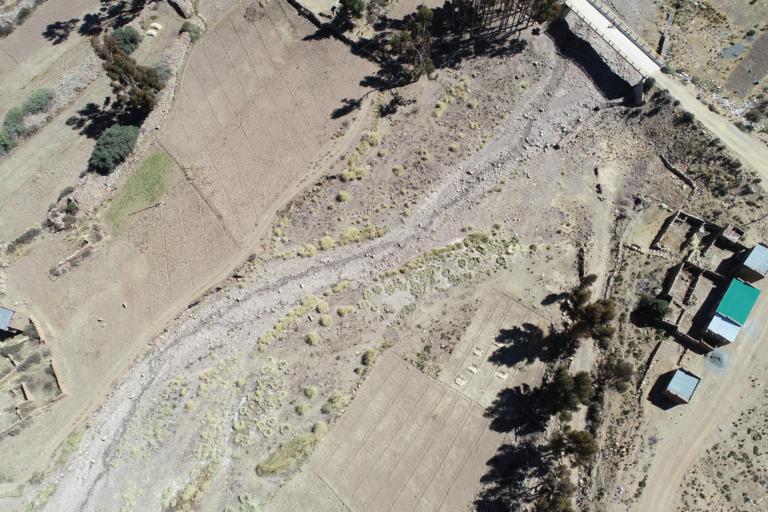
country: BO
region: La Paz
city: Achacachi
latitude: -15.8881
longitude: -68.8133
